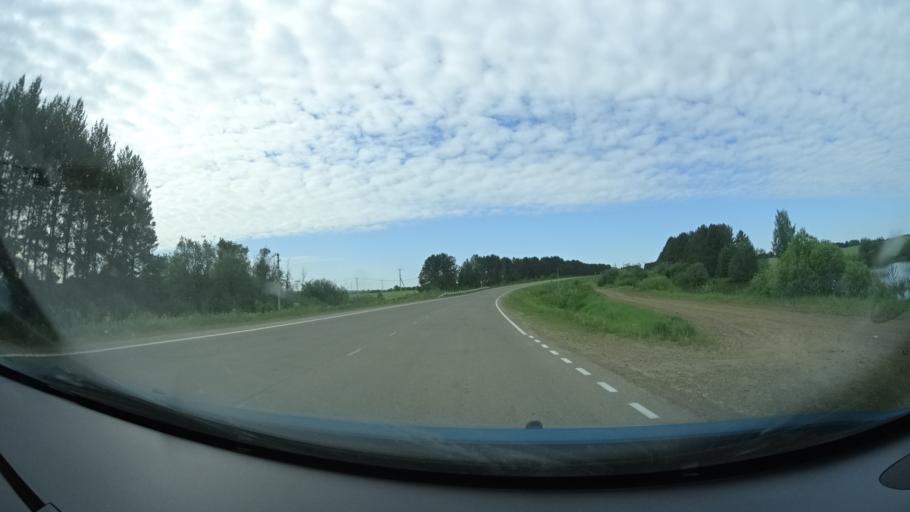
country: RU
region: Perm
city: Kuyeda
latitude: 56.4866
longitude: 55.5984
